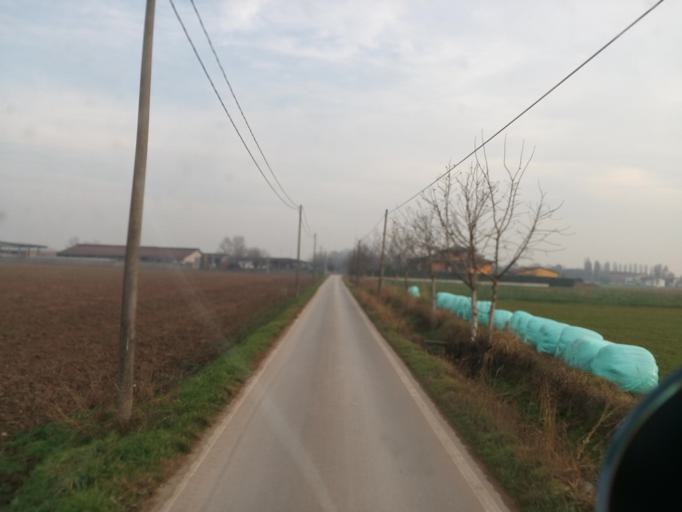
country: IT
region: Lombardy
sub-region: Provincia di Brescia
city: Vighizzolo
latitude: 45.4370
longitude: 10.3729
